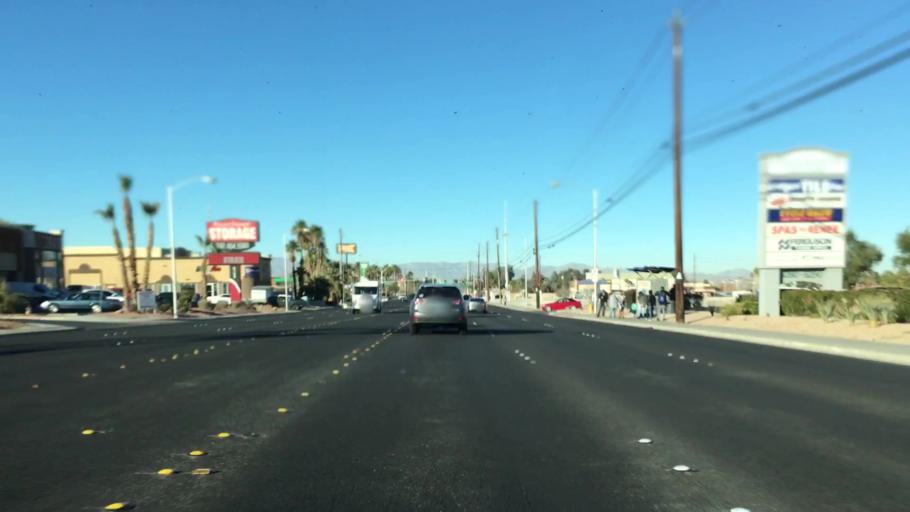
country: US
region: Nevada
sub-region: Clark County
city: Whitney
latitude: 36.0764
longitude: -115.1009
